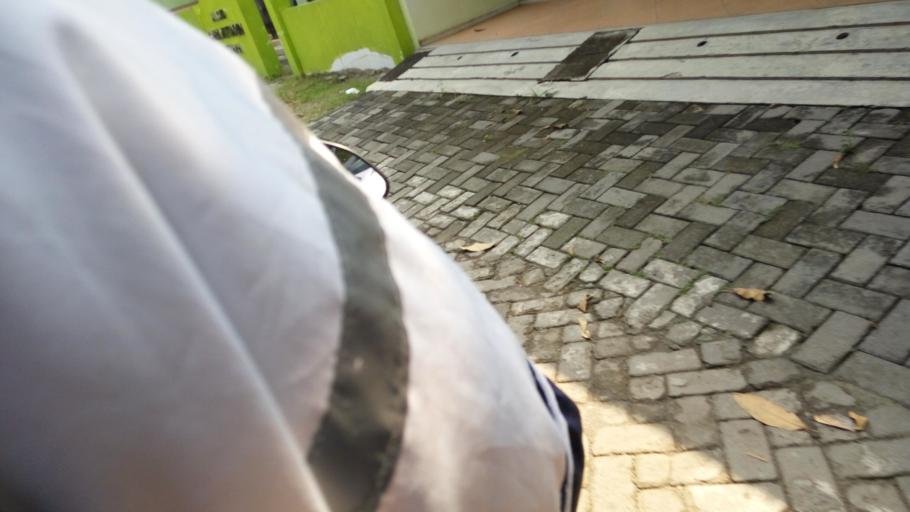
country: ID
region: Central Java
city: Mranggen
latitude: -7.0388
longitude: 110.4755
